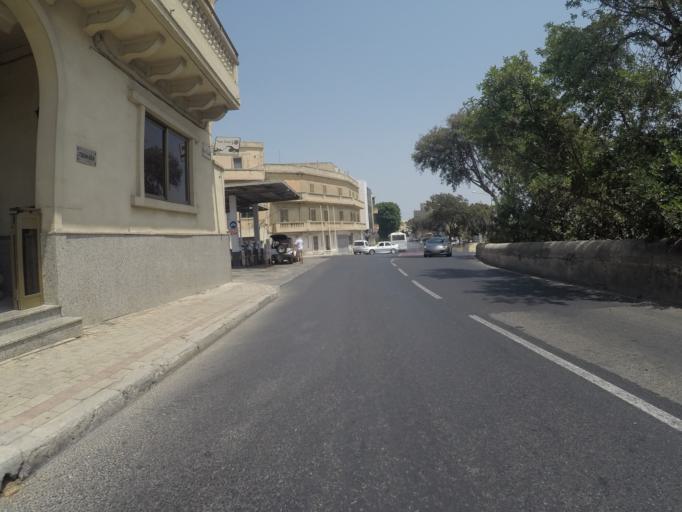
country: MT
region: Ir-Rabat
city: Rabat
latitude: 35.8820
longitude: 14.4021
